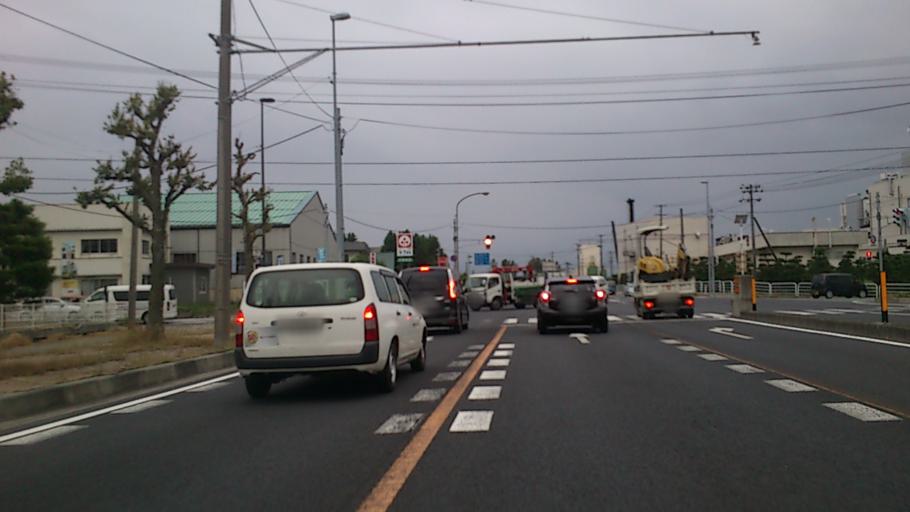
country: JP
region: Yamagata
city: Tendo
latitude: 38.3245
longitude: 140.3644
